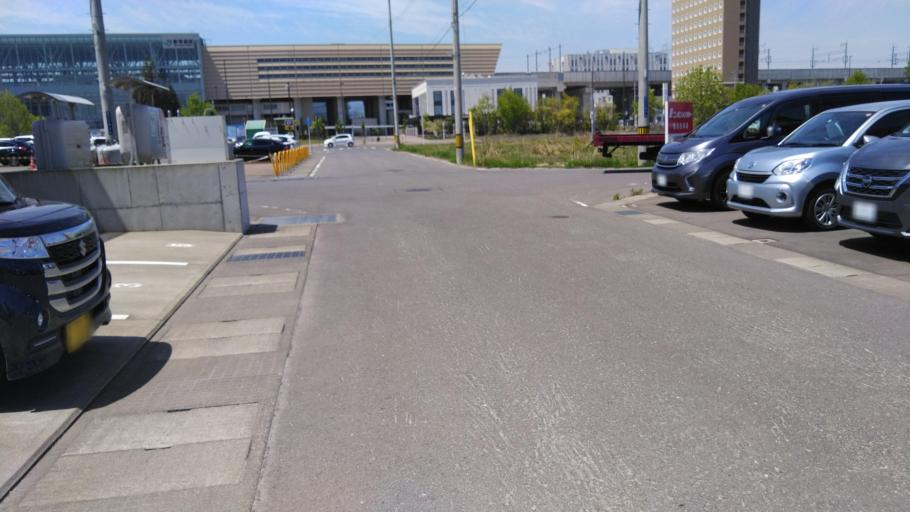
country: JP
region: Aomori
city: Aomori Shi
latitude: 40.8287
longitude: 140.6962
